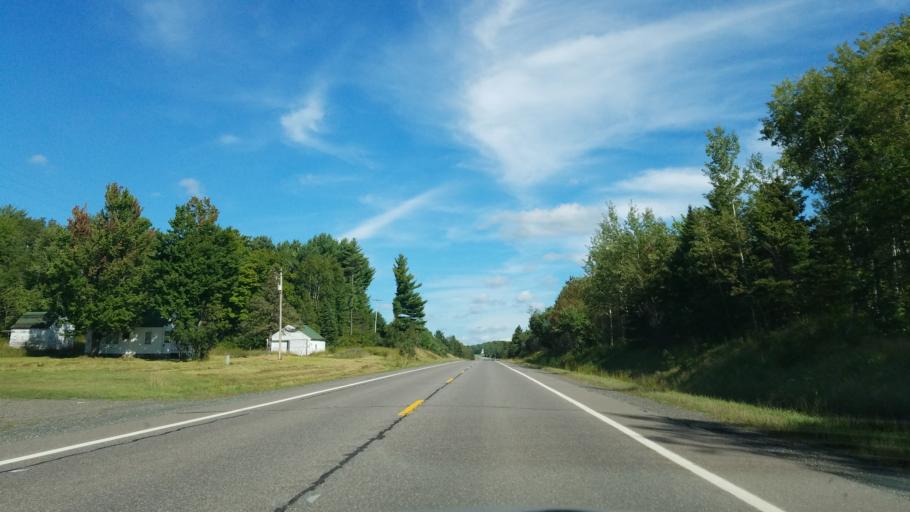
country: US
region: Michigan
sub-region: Baraga County
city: L'Anse
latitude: 46.5452
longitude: -88.5561
